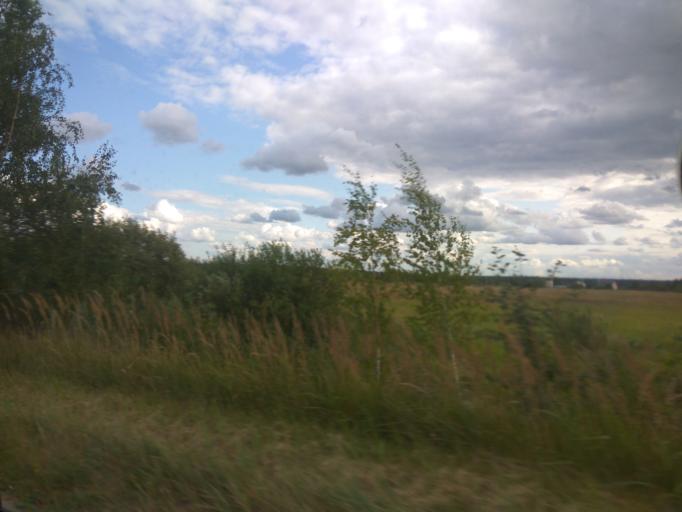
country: RU
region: Moskovskaya
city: Bronnitsy
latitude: 55.4542
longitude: 38.2590
